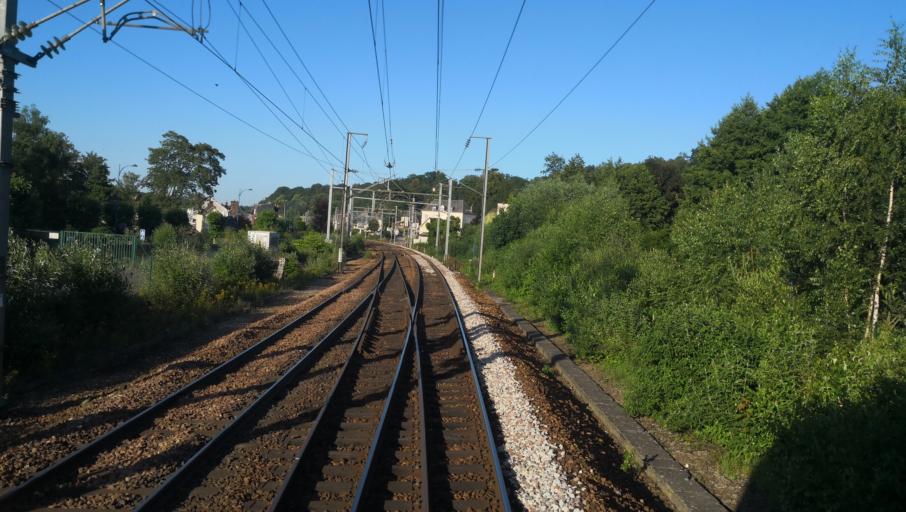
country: FR
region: Haute-Normandie
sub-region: Departement de l'Eure
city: Bernay
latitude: 49.0873
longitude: 0.5994
